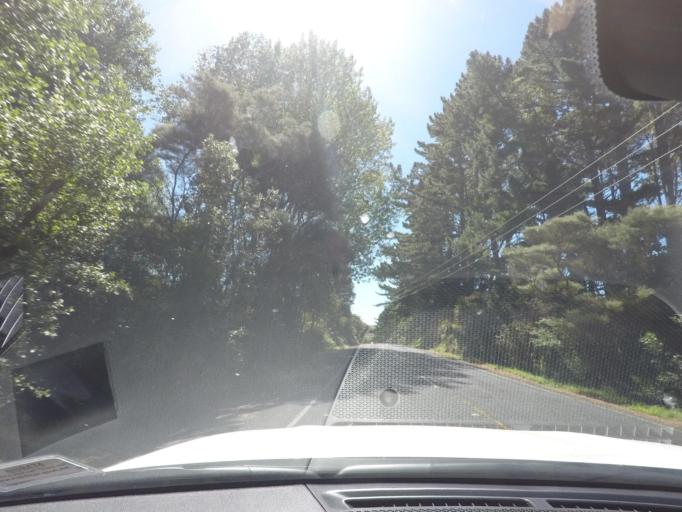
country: NZ
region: Auckland
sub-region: Auckland
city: Parakai
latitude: -36.6108
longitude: 174.3380
